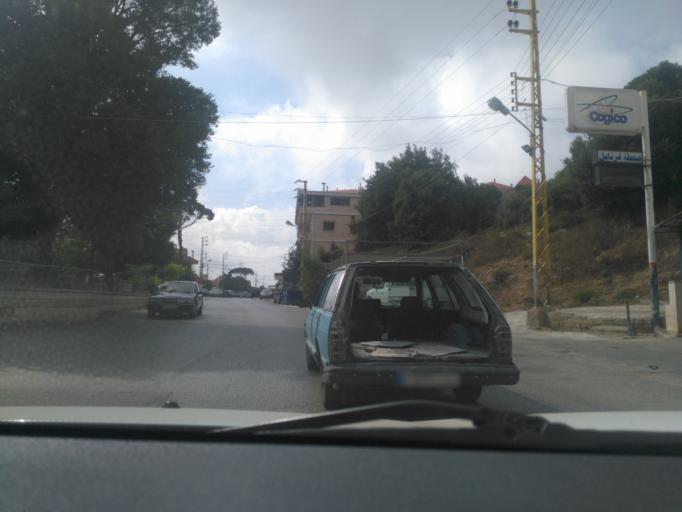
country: LB
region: Mont-Liban
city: Bhamdoun el Mhatta
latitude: 33.8495
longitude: 35.7279
